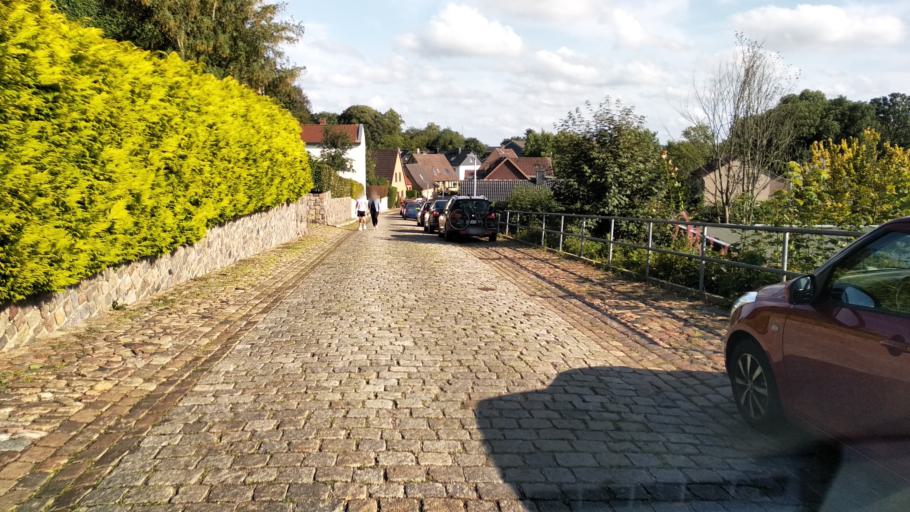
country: DE
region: Schleswig-Holstein
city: Schleswig
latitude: 54.5164
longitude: 9.5468
